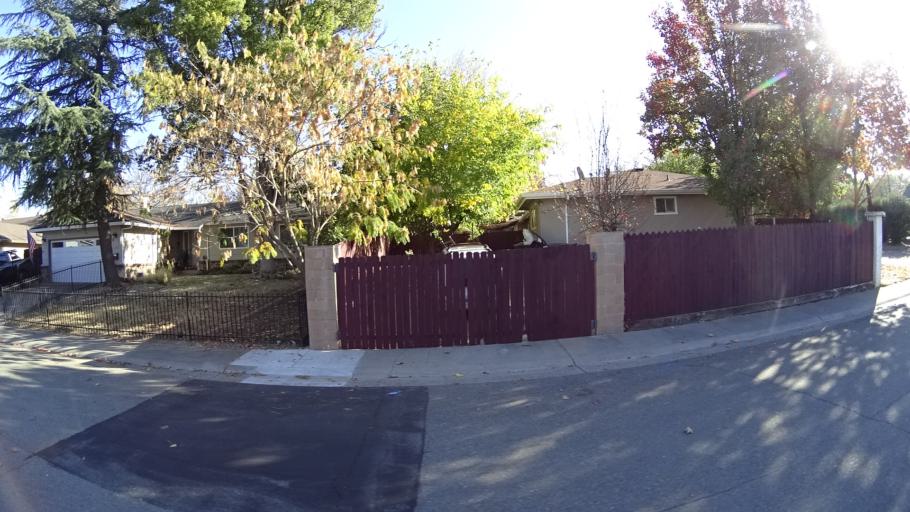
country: US
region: California
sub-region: Sacramento County
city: Fair Oaks
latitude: 38.6640
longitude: -121.2972
